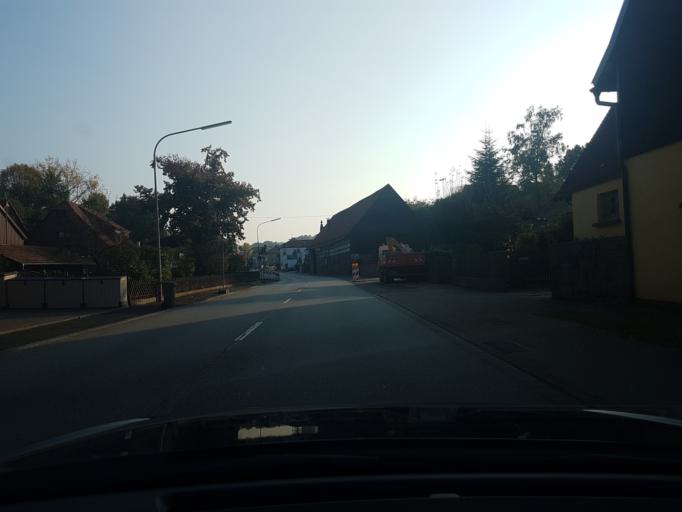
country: DE
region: Hesse
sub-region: Regierungsbezirk Darmstadt
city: Beerfelden
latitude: 49.5955
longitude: 8.9899
